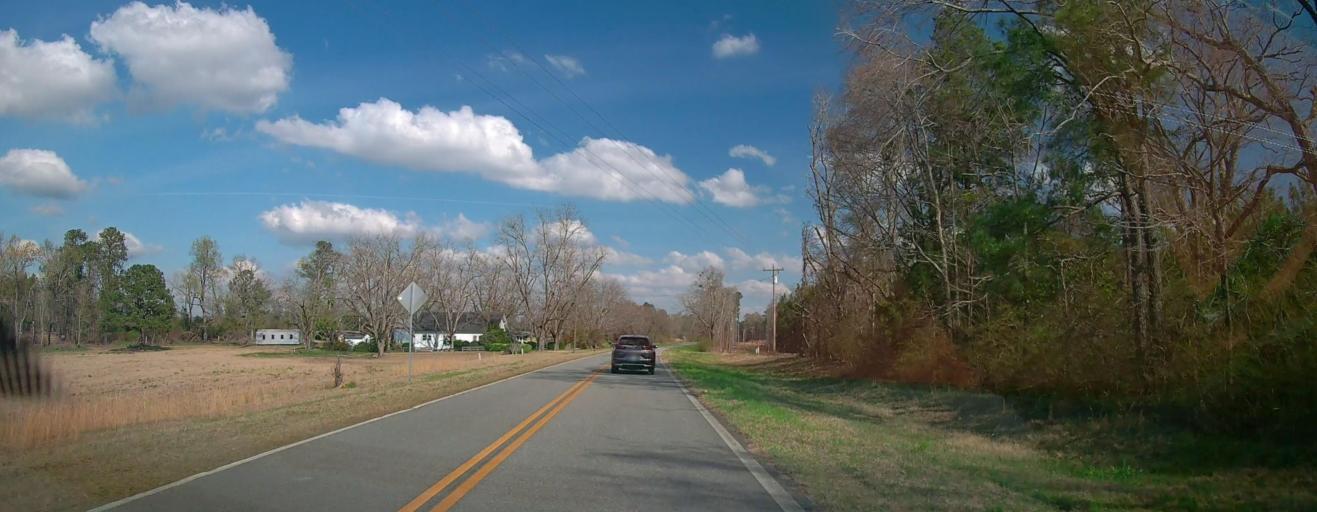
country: US
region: Georgia
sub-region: Wilkinson County
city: Irwinton
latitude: 32.6340
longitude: -83.1172
